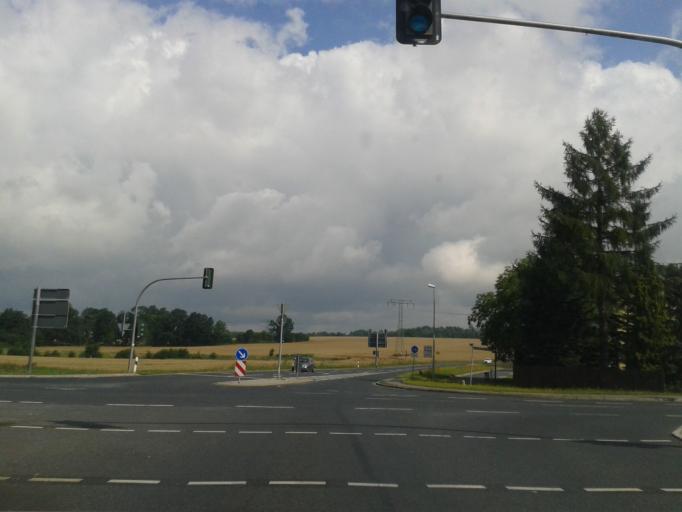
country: DE
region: Saxony
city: Radeberg
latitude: 51.1247
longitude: 13.9372
